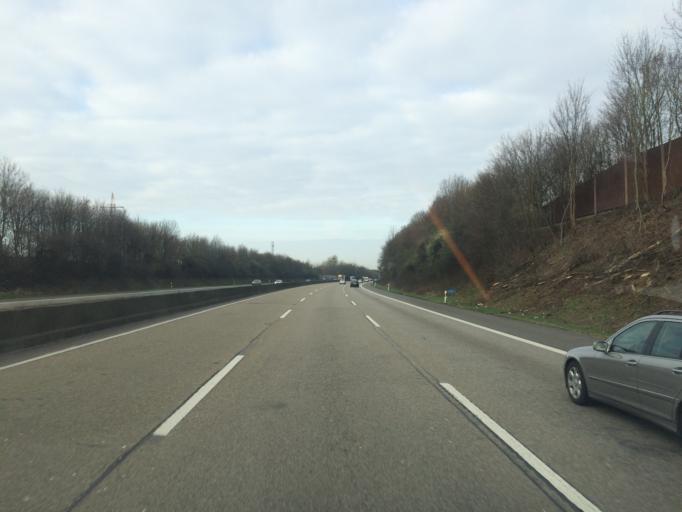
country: DE
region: North Rhine-Westphalia
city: Opladen
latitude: 51.0587
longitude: 7.0617
